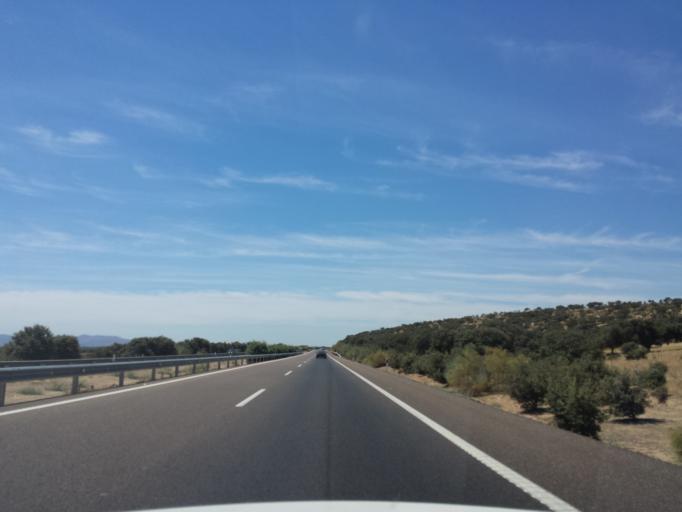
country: ES
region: Extremadura
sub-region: Provincia de Badajoz
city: San Pedro de Merida
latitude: 38.9648
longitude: -6.1549
